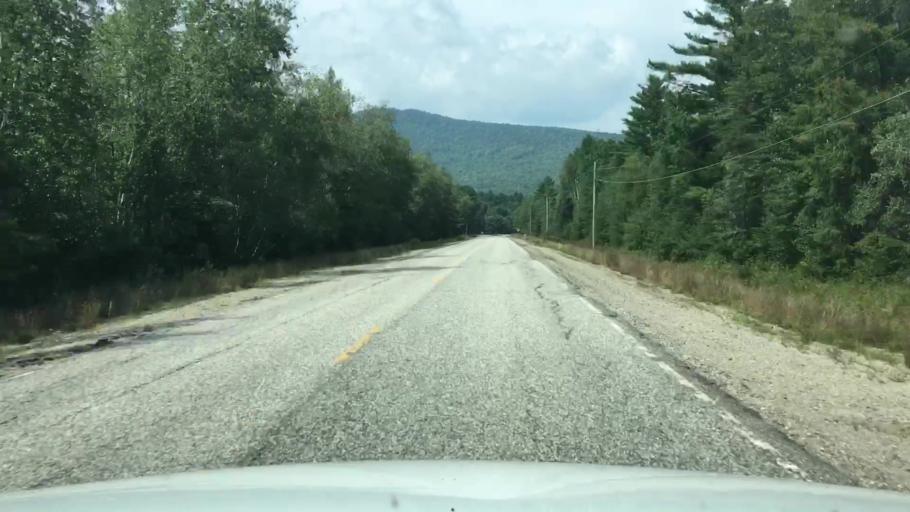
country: US
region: Maine
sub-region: Oxford County
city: Rumford
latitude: 44.5771
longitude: -70.7286
